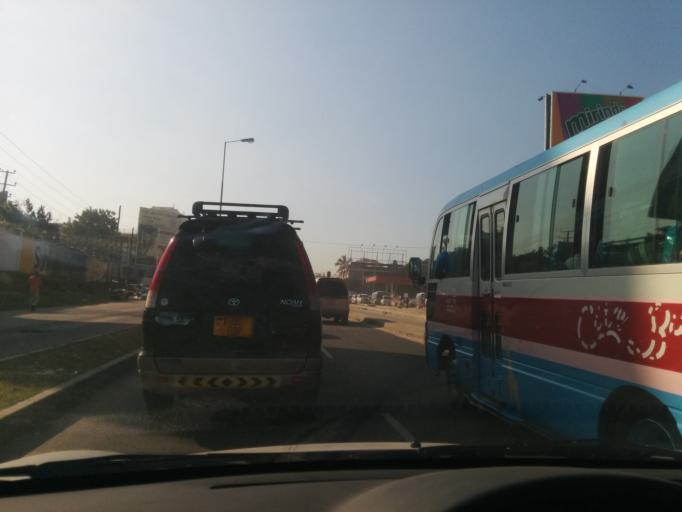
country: TZ
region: Dar es Salaam
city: Dar es Salaam
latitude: -6.8125
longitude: 39.2725
